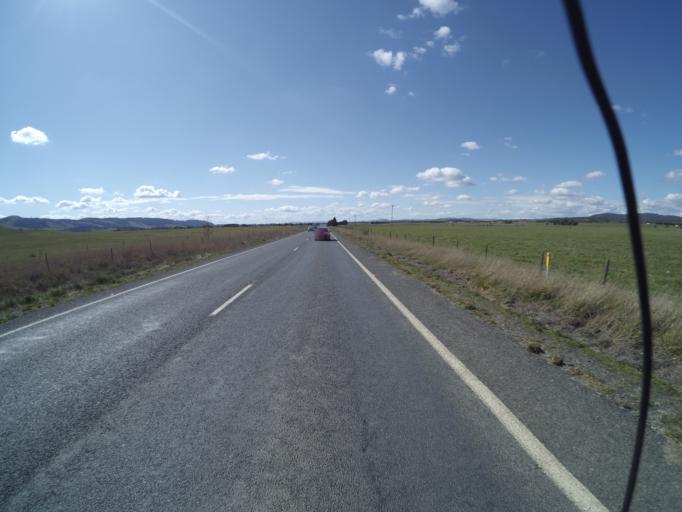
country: AU
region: New South Wales
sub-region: Palerang
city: Bungendore
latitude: -35.2851
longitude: 149.4215
